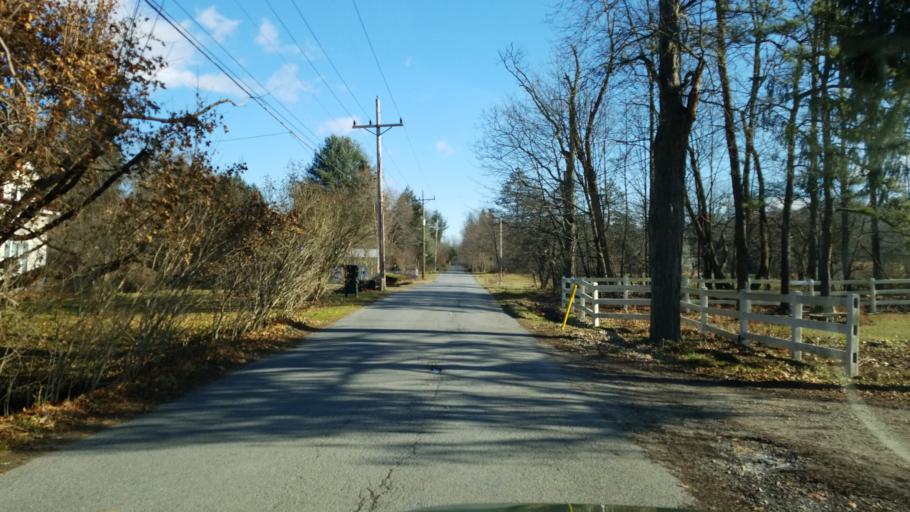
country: US
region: Pennsylvania
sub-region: Clearfield County
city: Hyde
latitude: 40.9823
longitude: -78.4891
